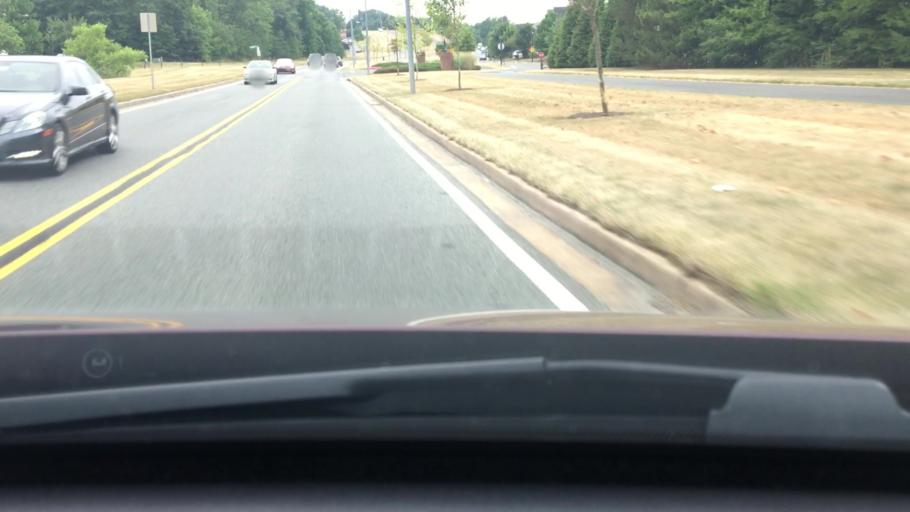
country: US
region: Maryland
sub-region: Prince George's County
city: Calverton
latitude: 39.0707
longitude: -76.9209
